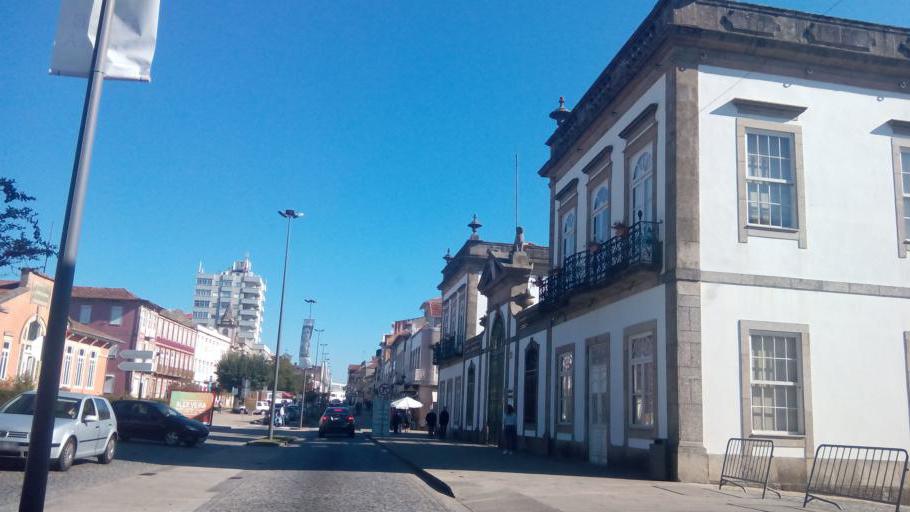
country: PT
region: Porto
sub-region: Penafiel
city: Penafiel
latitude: 41.2033
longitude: -8.2873
